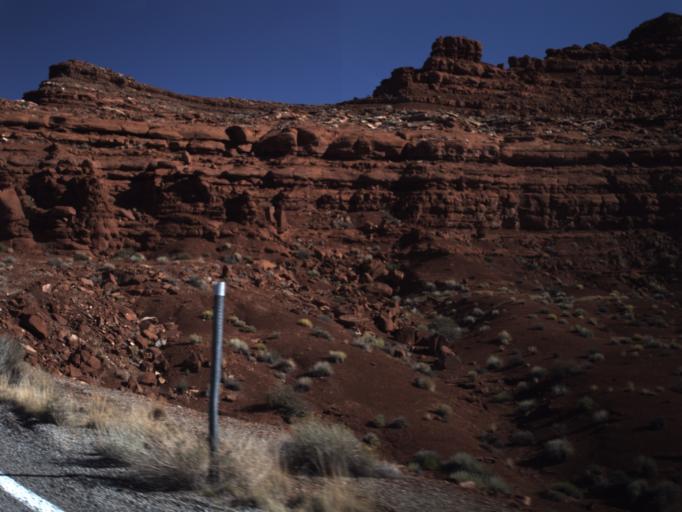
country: US
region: Utah
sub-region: San Juan County
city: Blanding
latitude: 37.8546
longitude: -110.3531
